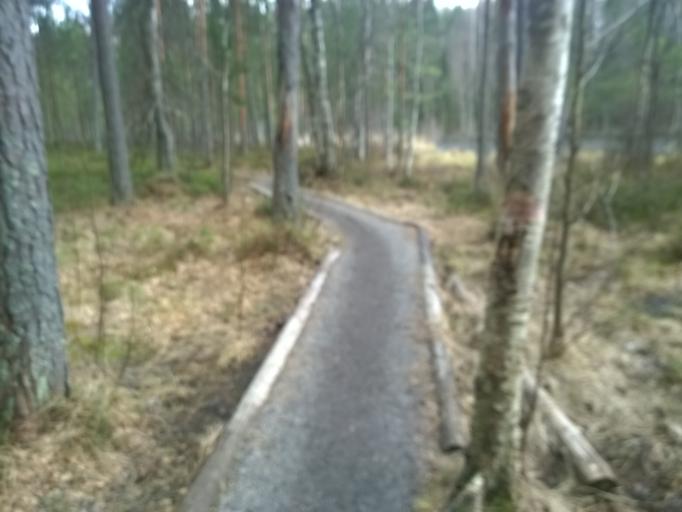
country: FI
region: Pirkanmaa
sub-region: Tampere
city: Tampere
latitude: 61.4395
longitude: 23.8331
